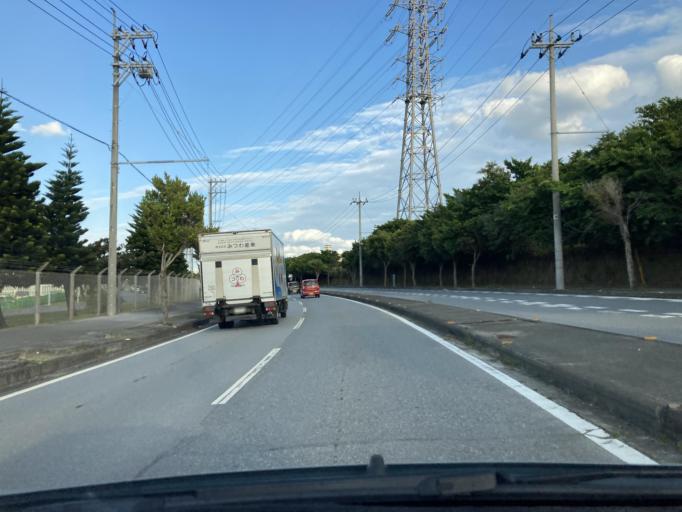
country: JP
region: Okinawa
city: Chatan
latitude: 26.3055
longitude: 127.7739
